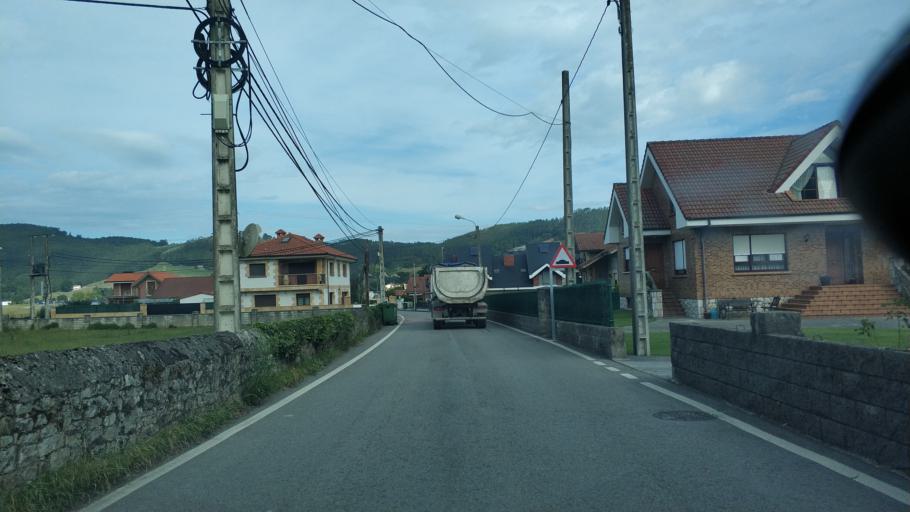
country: ES
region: Cantabria
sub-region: Provincia de Cantabria
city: Santa Maria de Cayon
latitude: 43.3079
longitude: -3.8763
